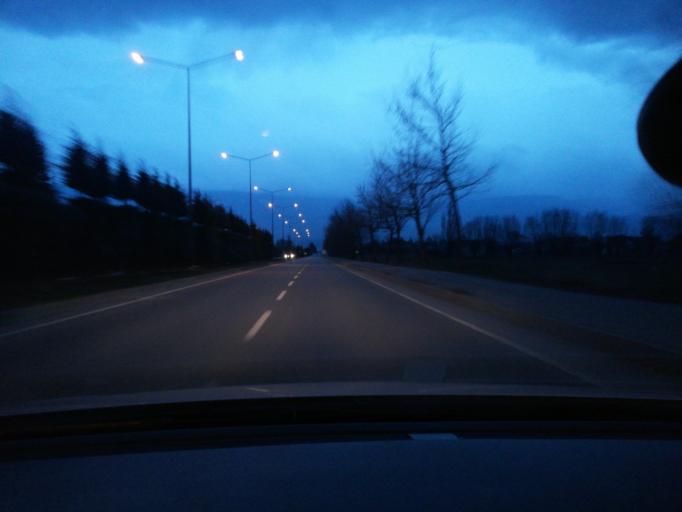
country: TR
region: Bolu
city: Bolu
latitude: 40.7171
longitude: 31.6144
